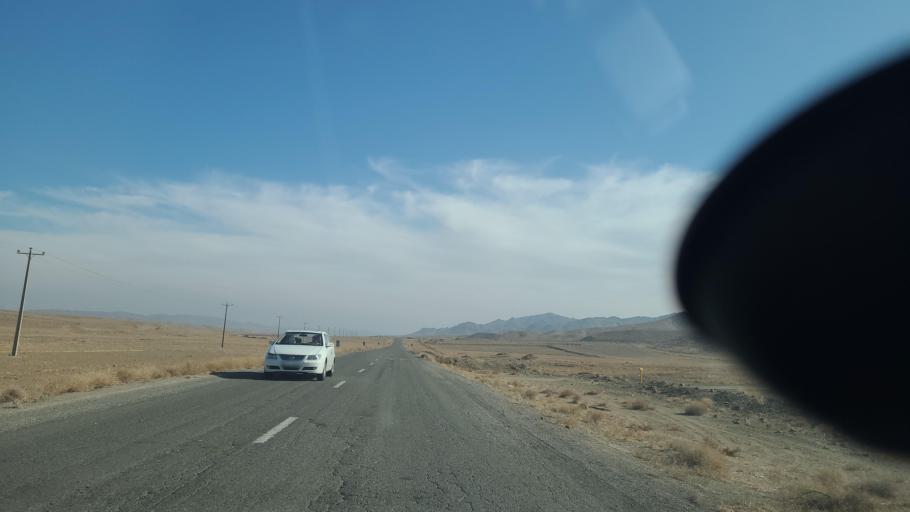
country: IR
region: Razavi Khorasan
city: Fariman
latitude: 35.5882
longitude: 59.6326
